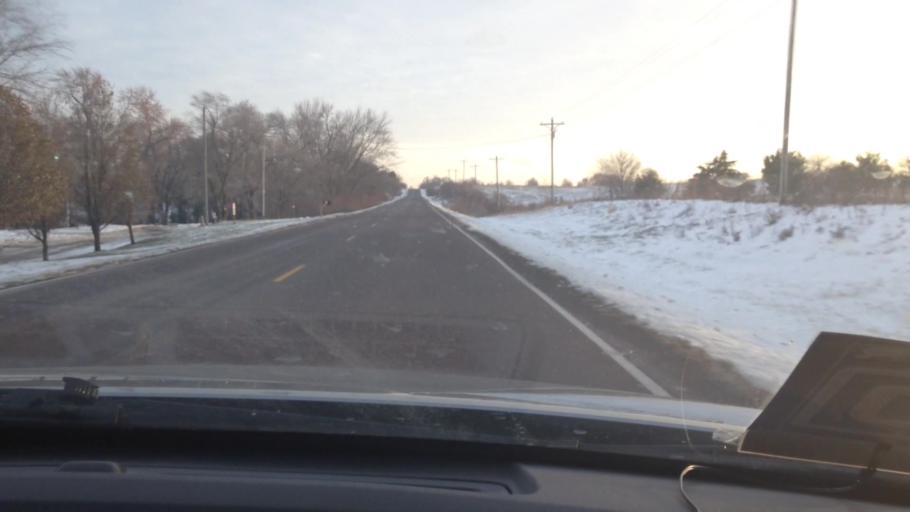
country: US
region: Kansas
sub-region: Leavenworth County
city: Lansing
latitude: 39.2246
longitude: -94.9846
